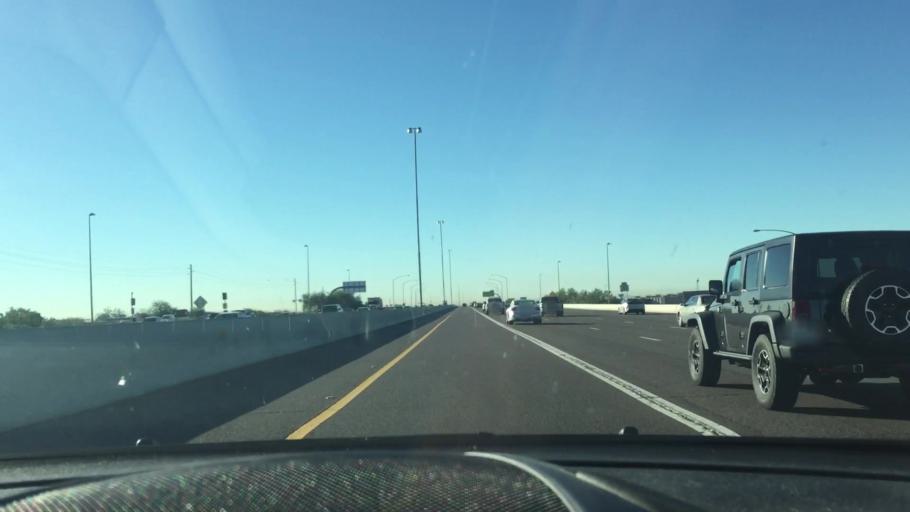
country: US
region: Arizona
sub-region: Maricopa County
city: Paradise Valley
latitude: 33.6336
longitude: -111.8914
